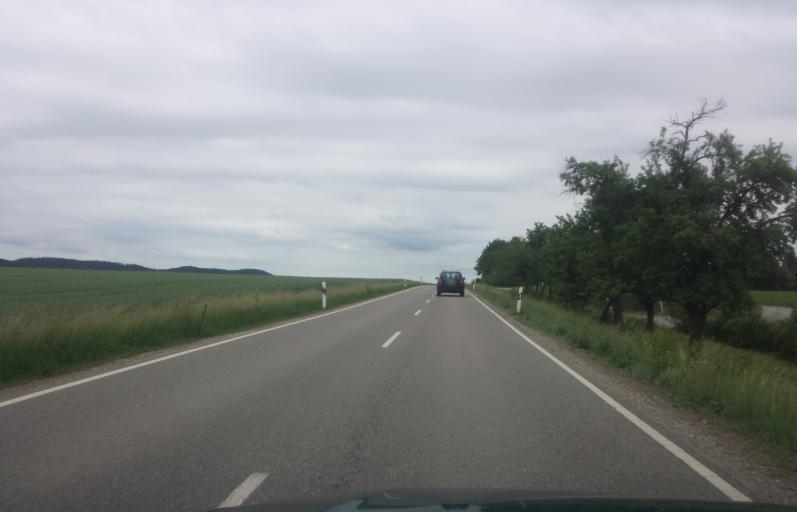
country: DE
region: Bavaria
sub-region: Regierungsbezirk Mittelfranken
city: Weigenheim
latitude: 49.5591
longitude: 10.2928
